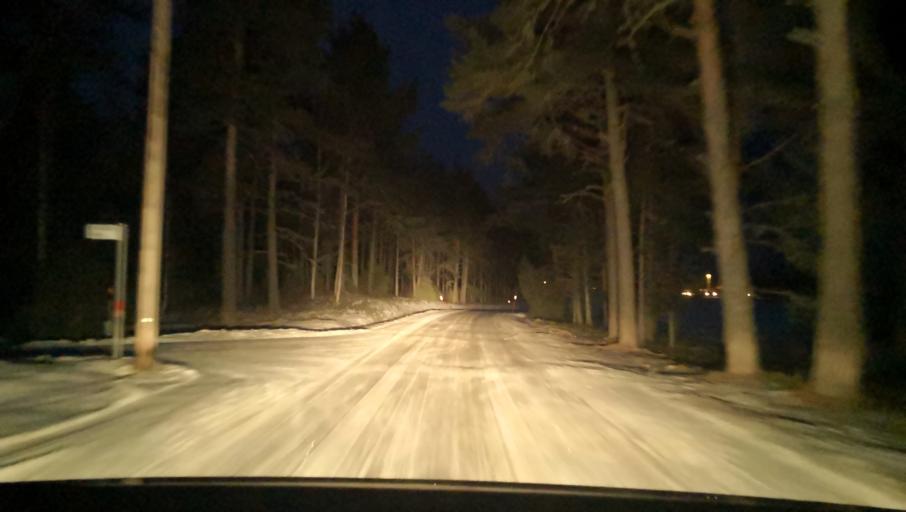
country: SE
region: Uppsala
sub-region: Heby Kommun
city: Tarnsjo
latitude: 60.2949
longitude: 16.8047
